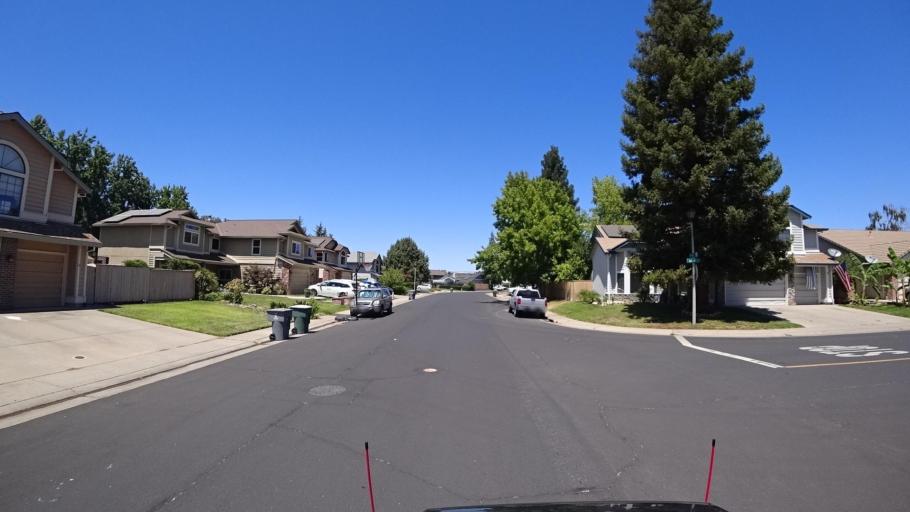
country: US
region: California
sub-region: Placer County
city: Rocklin
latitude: 38.8113
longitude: -121.2746
